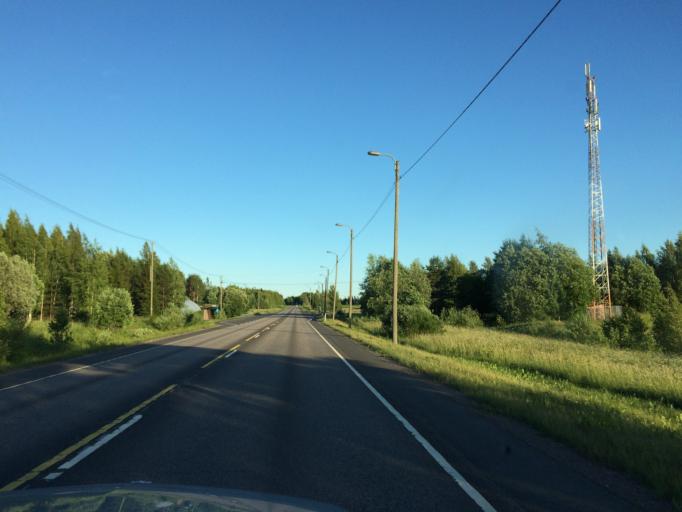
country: FI
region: Haeme
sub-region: Haemeenlinna
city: Tervakoski
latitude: 60.8152
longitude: 24.6432
